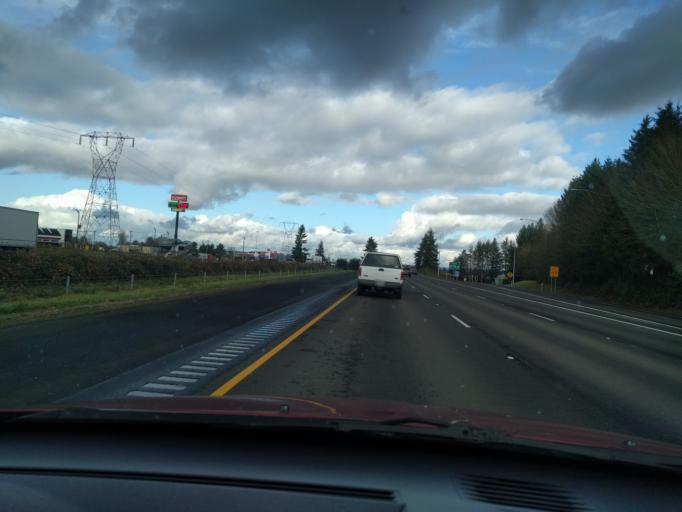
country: US
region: Oregon
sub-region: Marion County
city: Hubbard
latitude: 45.2323
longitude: -122.8089
